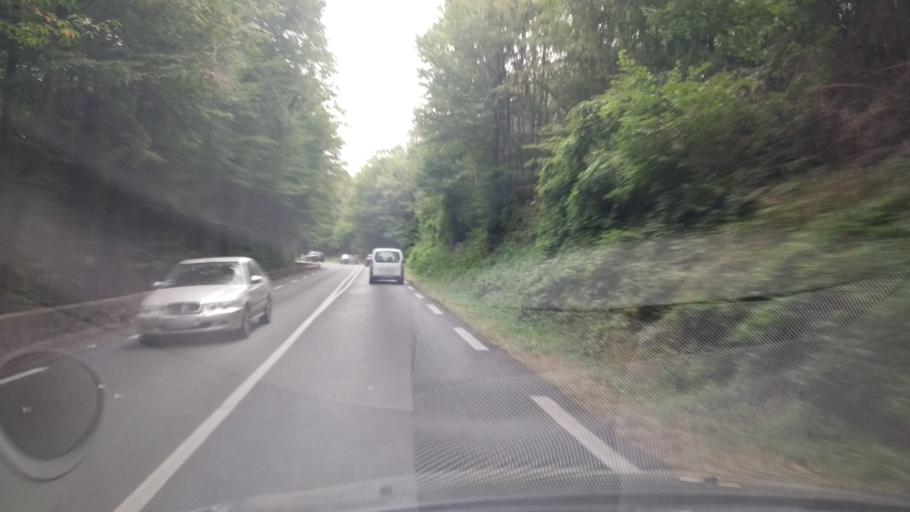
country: FR
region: Poitou-Charentes
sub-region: Departement de la Vienne
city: Saint-Benoit
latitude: 46.5474
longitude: 0.3515
